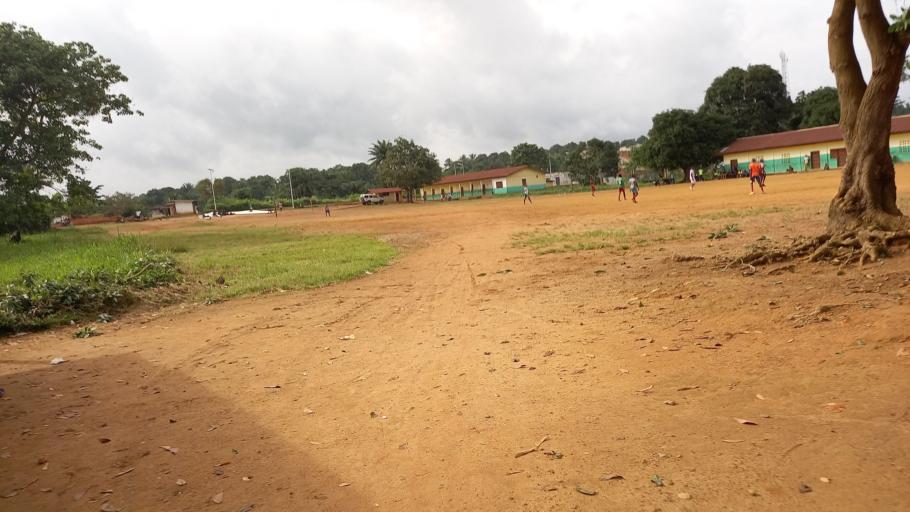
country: SL
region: Eastern Province
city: Kailahun
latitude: 8.2753
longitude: -10.5807
